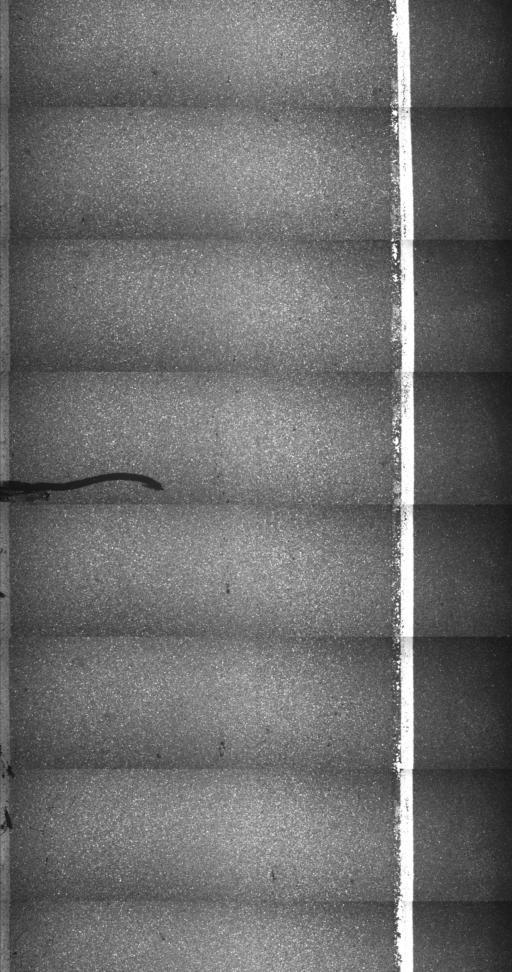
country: CA
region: Quebec
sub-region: Estrie
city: Coaticook
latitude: 44.9726
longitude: -71.8169
